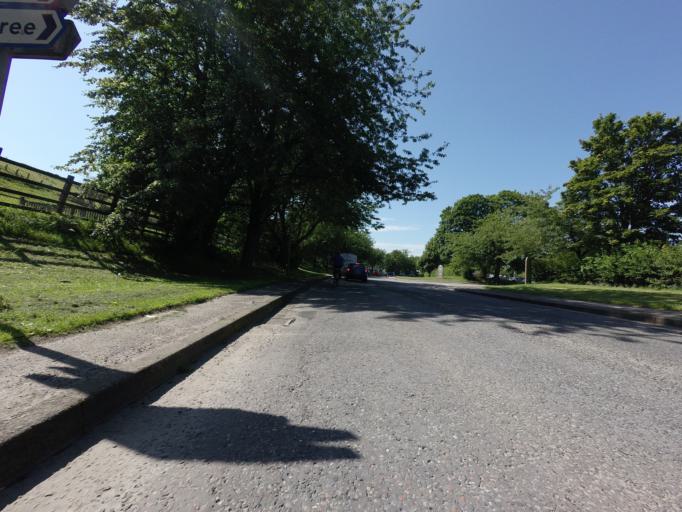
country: GB
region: Scotland
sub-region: Highland
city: Dingwall
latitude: 57.5939
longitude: -4.4288
